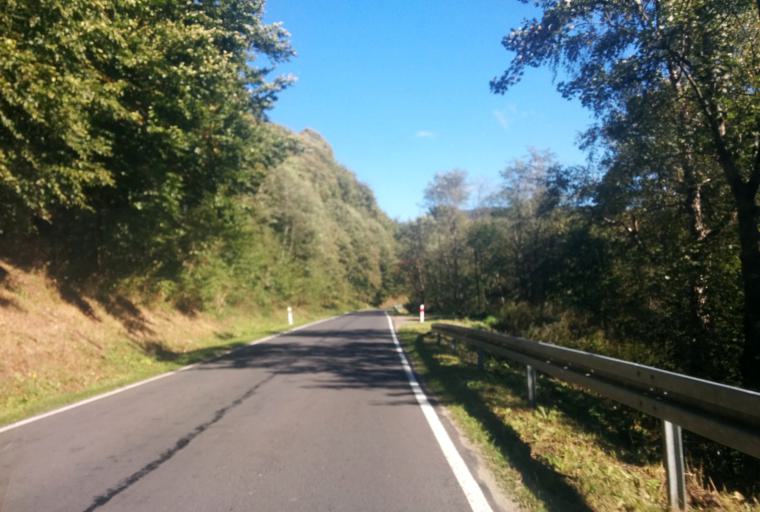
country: PL
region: Subcarpathian Voivodeship
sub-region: Powiat bieszczadzki
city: Lutowiska
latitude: 49.1182
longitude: 22.6639
